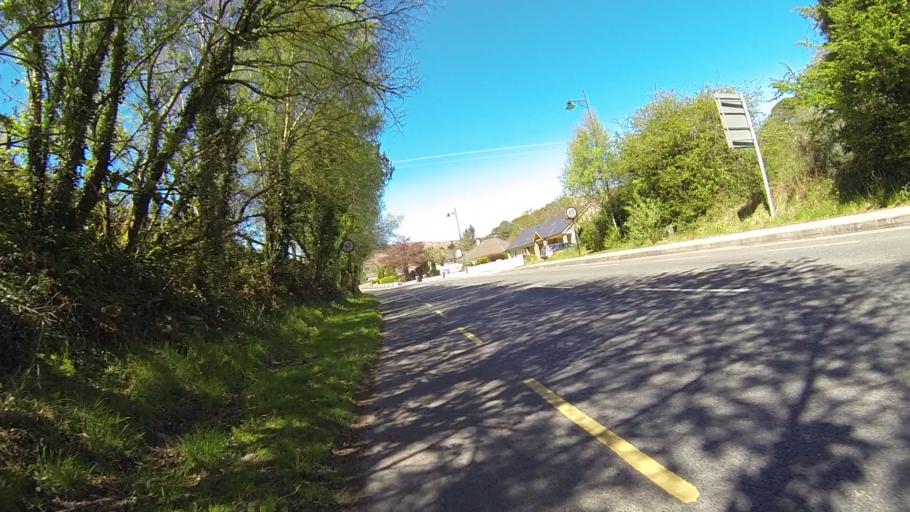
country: IE
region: Munster
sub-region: Ciarrai
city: Kenmare
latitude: 51.8849
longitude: -9.5926
